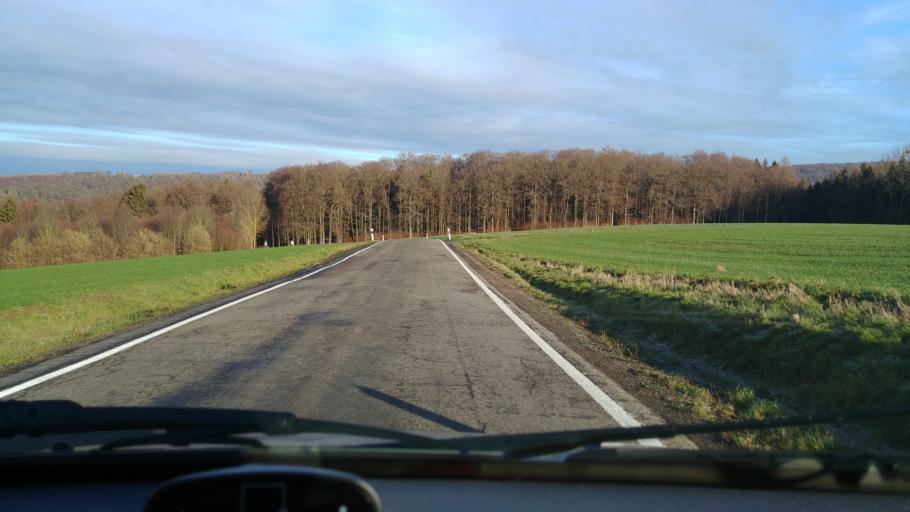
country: DE
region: Rheinland-Pfalz
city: Lollschied
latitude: 50.2740
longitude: 7.8612
